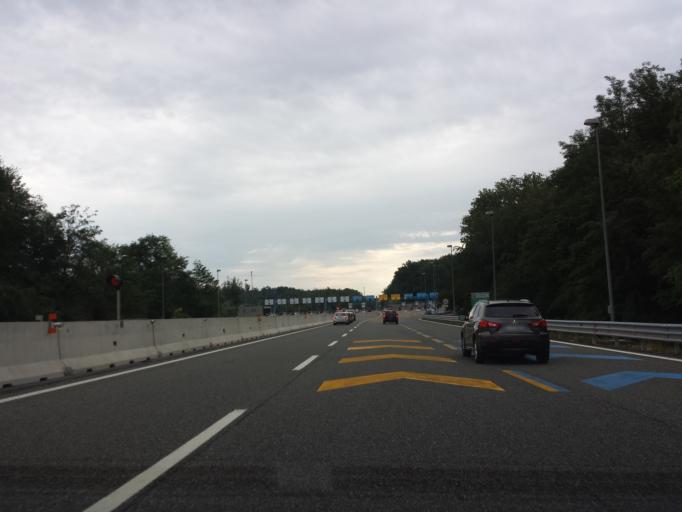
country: IT
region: Lombardy
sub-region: Provincia di Varese
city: Besnate
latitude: 45.6894
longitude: 8.7730
